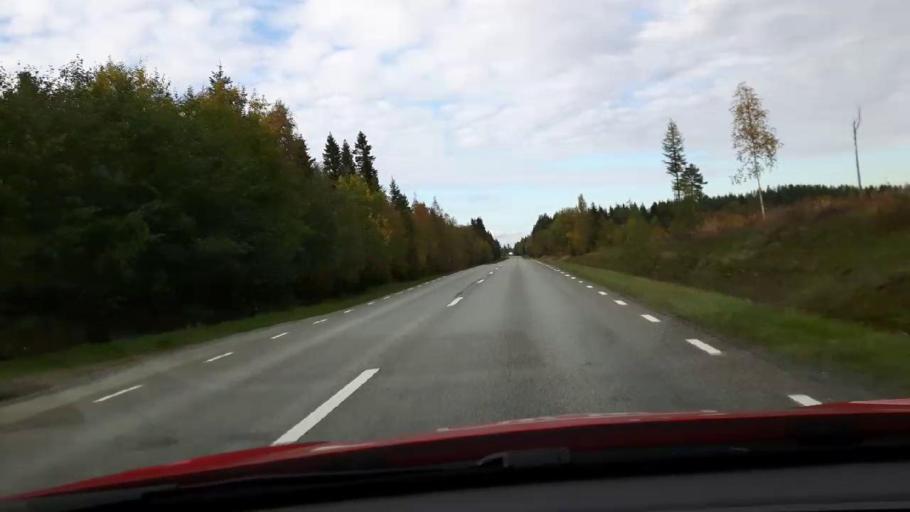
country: SE
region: Jaemtland
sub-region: Krokoms Kommun
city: Valla
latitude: 63.2305
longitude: 14.0129
